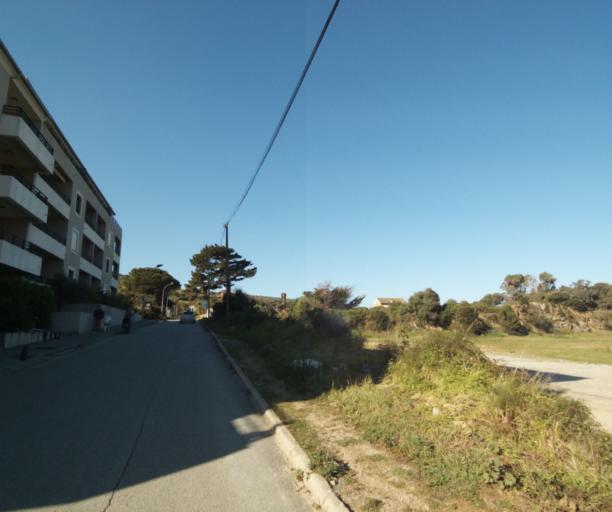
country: FR
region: Corsica
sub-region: Departement de la Corse-du-Sud
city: Propriano
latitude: 41.6743
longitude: 8.8978
